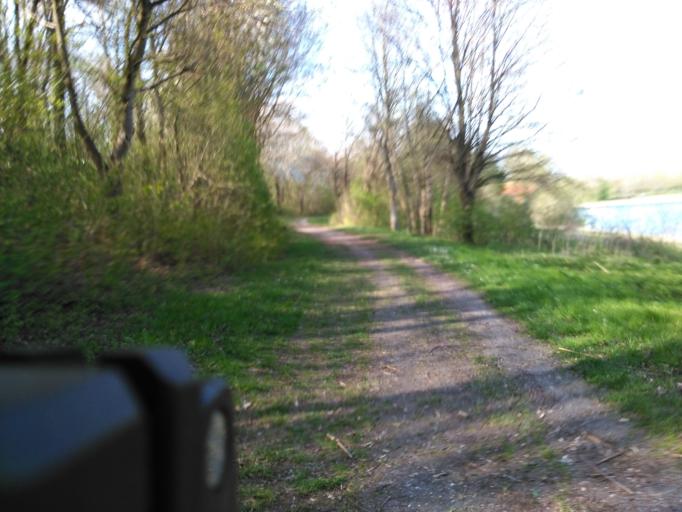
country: DE
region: Bavaria
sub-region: Upper Bavaria
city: Mammendorf
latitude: 48.1995
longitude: 11.1668
